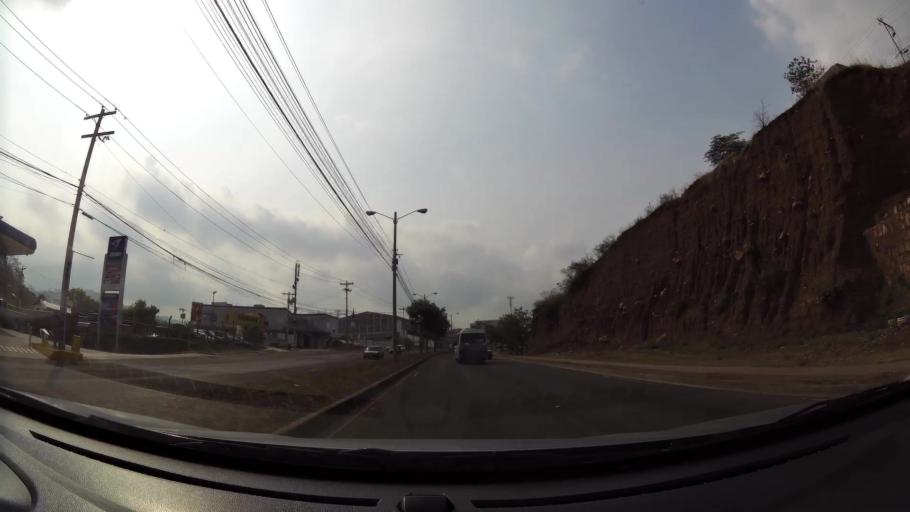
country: HN
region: Francisco Morazan
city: Santa Lucia
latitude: 14.1057
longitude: -87.1613
